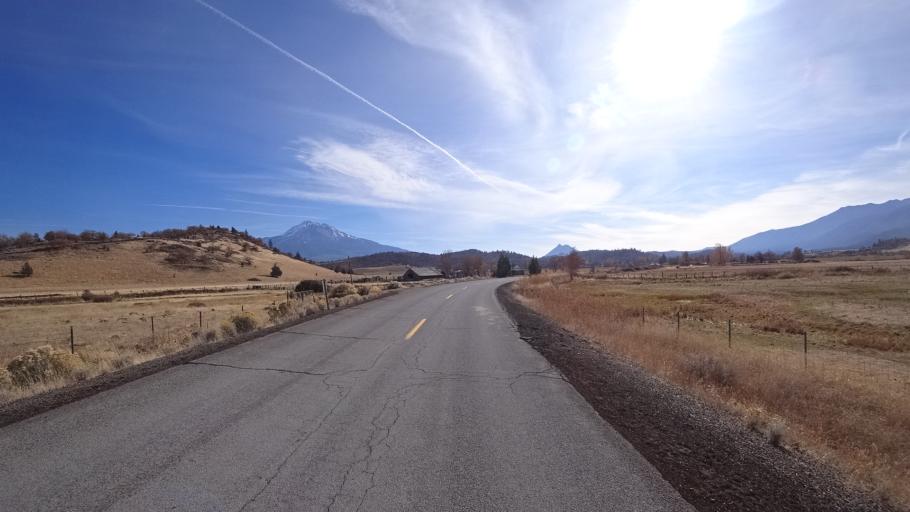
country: US
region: California
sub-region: Siskiyou County
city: Weed
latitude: 41.4700
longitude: -122.4361
